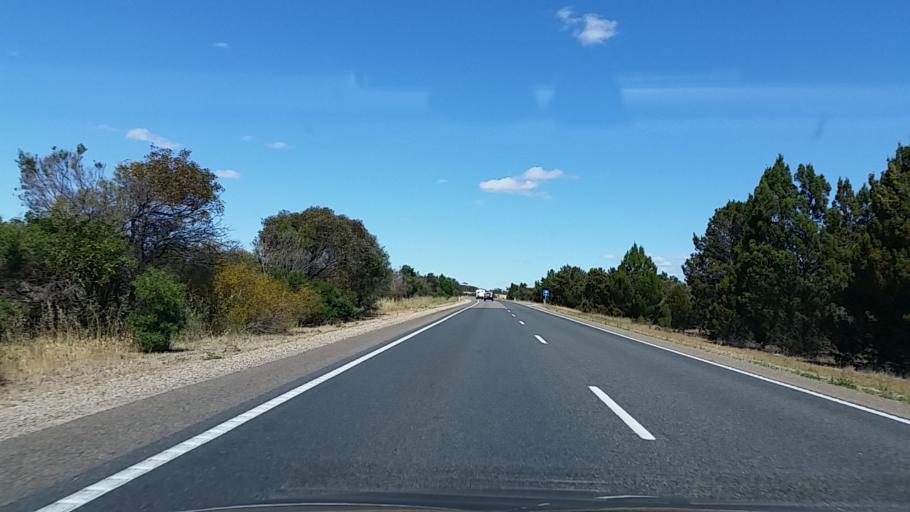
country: AU
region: South Australia
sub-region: Murray Bridge
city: Tailem Bend
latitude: -35.2131
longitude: 139.4101
